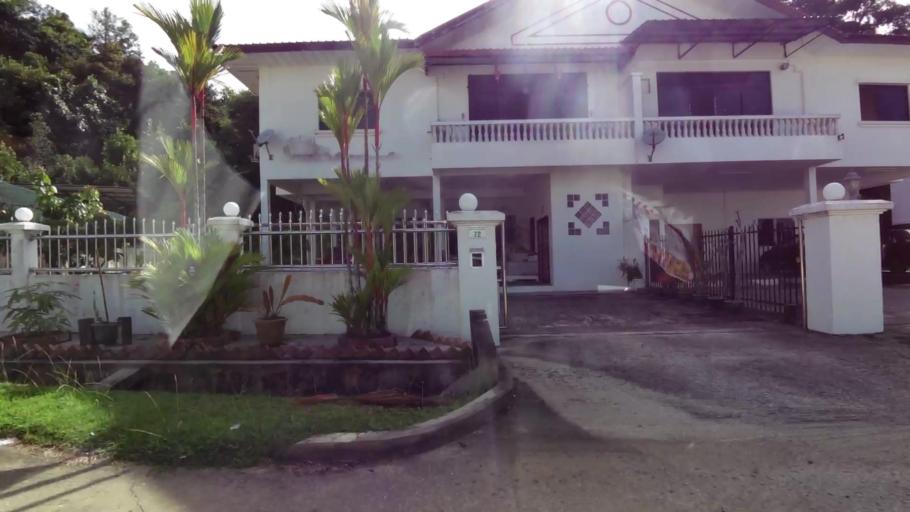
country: BN
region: Brunei and Muara
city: Bandar Seri Begawan
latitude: 4.9039
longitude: 114.9696
